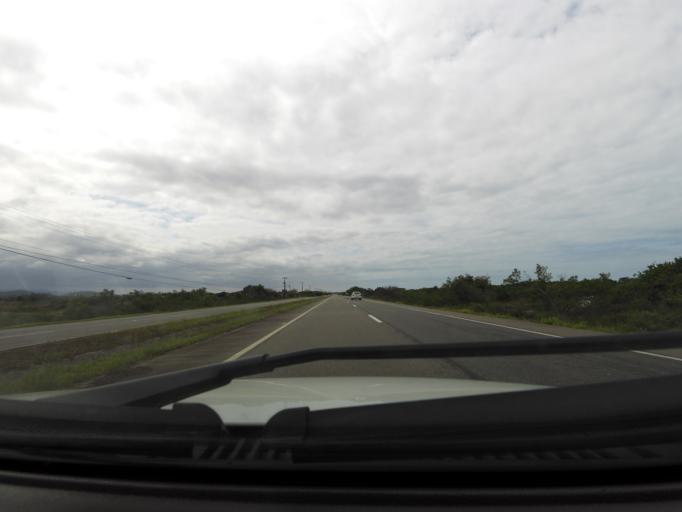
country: BR
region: Espirito Santo
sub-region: Guarapari
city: Guarapari
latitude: -20.5743
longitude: -40.4138
